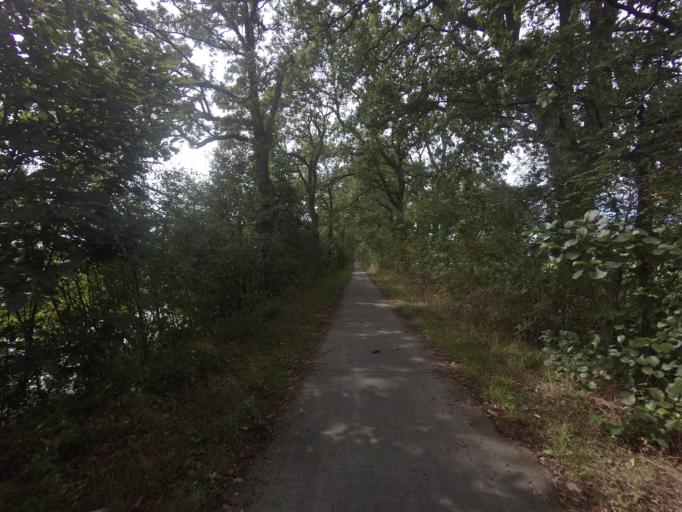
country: NL
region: Drenthe
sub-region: Gemeente Westerveld
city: Dwingeloo
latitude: 52.9632
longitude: 6.3645
